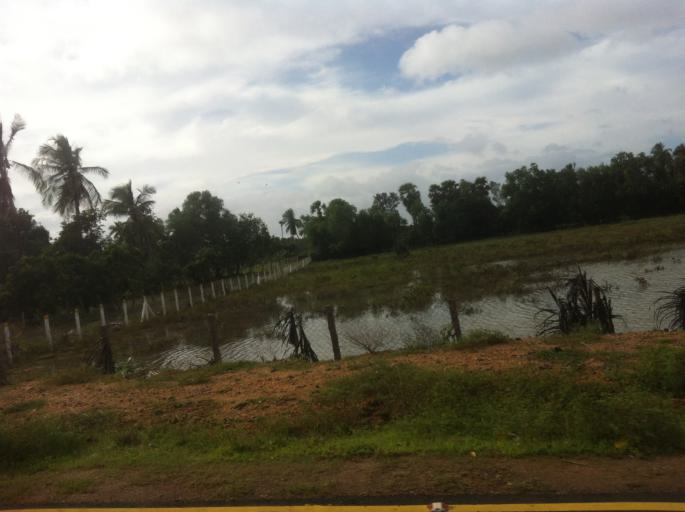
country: IN
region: Tamil Nadu
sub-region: Kancheepuram
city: Cheyyur
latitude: 12.3161
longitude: 80.0300
